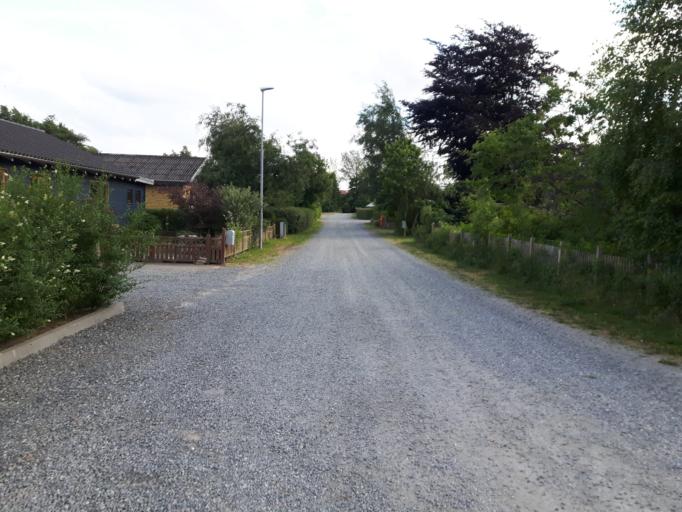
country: DK
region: Central Jutland
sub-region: Skive Kommune
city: Skive
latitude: 56.5535
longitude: 9.0575
